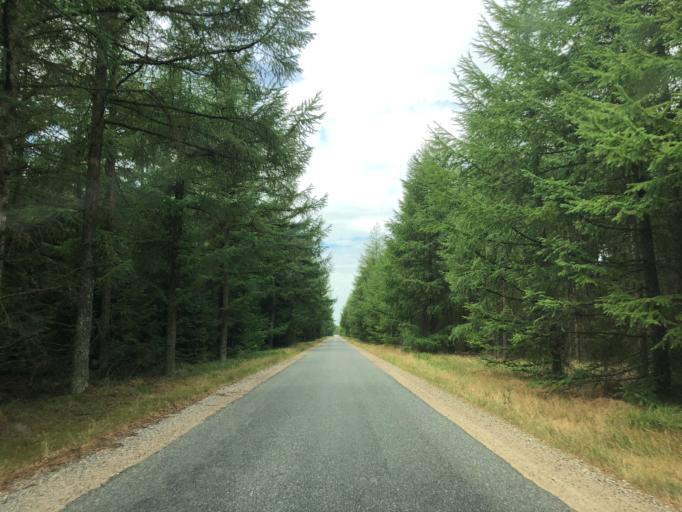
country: DK
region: South Denmark
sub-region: Billund Kommune
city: Grindsted
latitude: 55.6475
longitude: 8.8994
